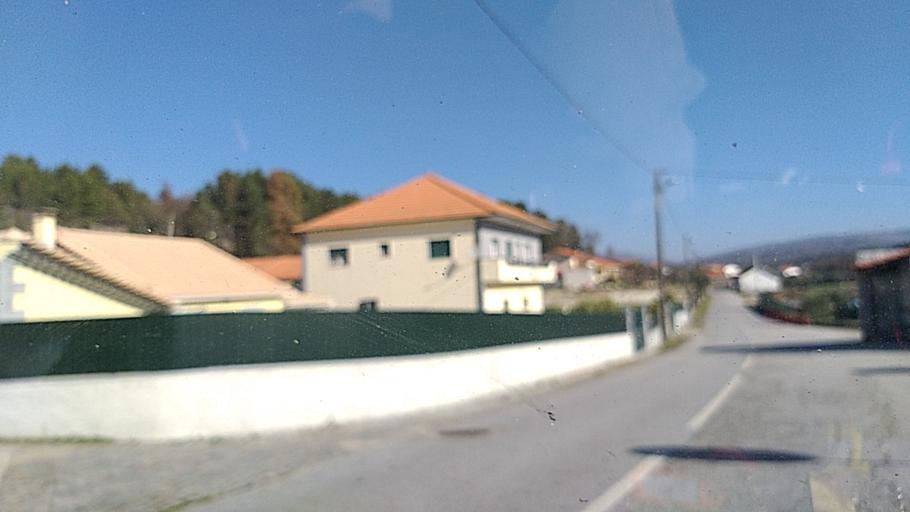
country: PT
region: Guarda
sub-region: Celorico da Beira
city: Celorico da Beira
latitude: 40.6502
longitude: -7.4663
